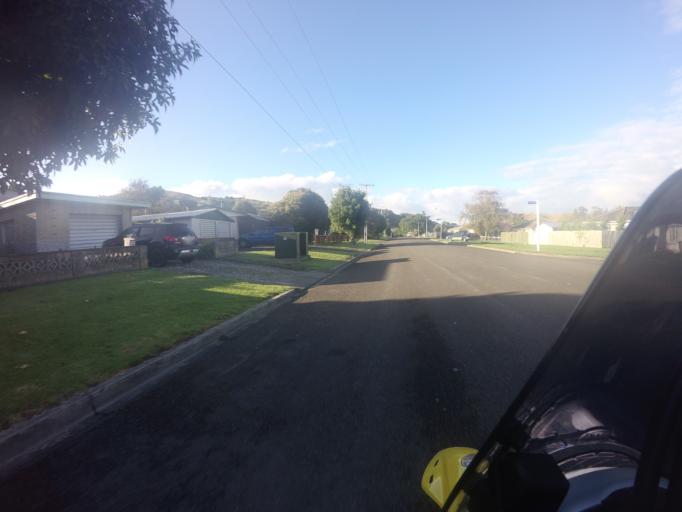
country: NZ
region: Gisborne
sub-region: Gisborne District
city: Gisborne
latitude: -38.6726
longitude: 178.0581
